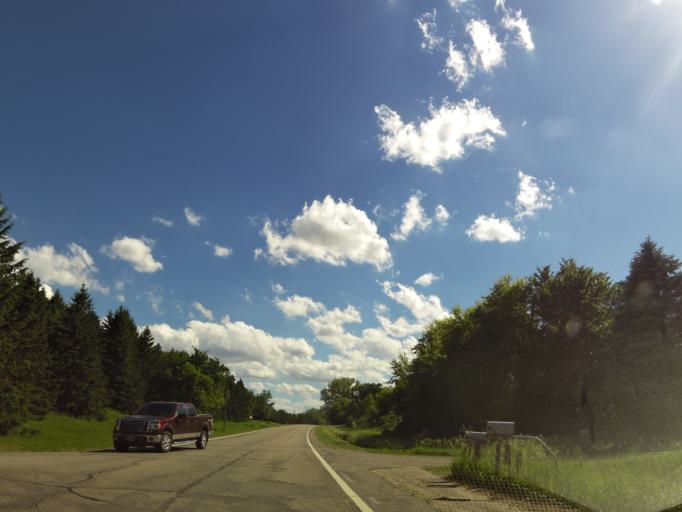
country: US
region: Minnesota
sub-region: Meeker County
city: Dassel
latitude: 45.1084
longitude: -94.3019
